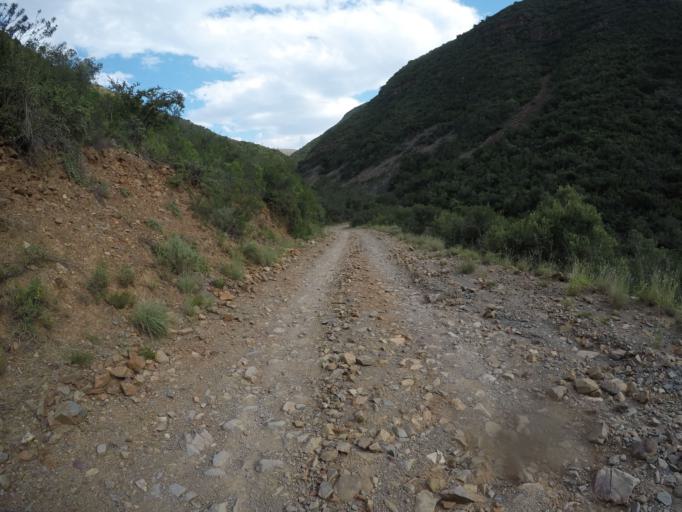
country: ZA
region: Eastern Cape
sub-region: Cacadu District Municipality
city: Kareedouw
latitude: -33.6499
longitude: 24.3363
